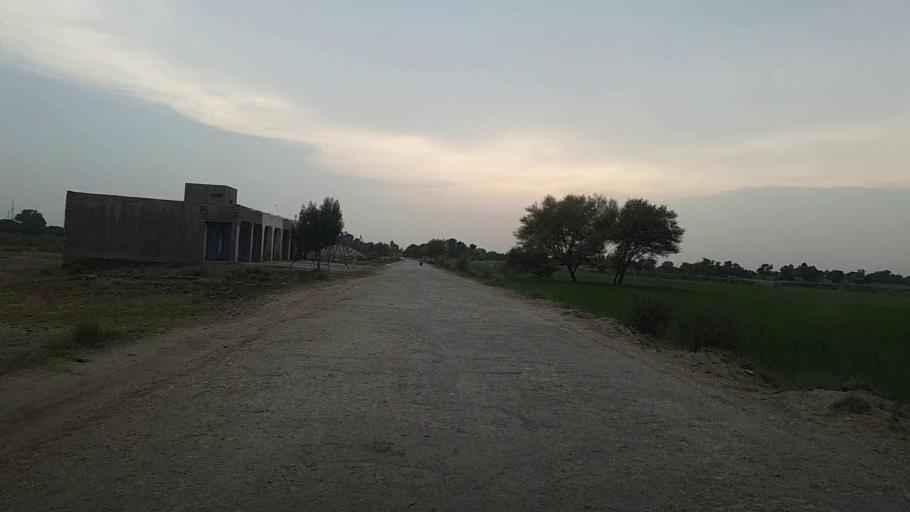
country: PK
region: Sindh
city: Khanpur
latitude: 27.8475
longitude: 69.4248
